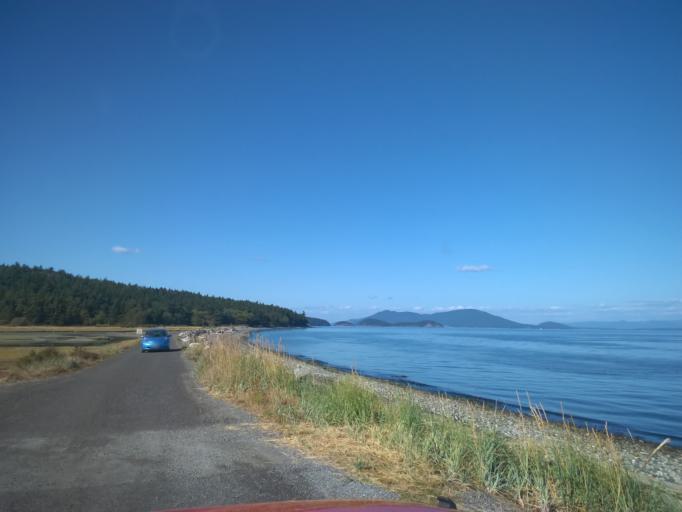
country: US
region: Washington
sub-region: Island County
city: Ault Field
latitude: 48.4599
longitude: -122.8202
